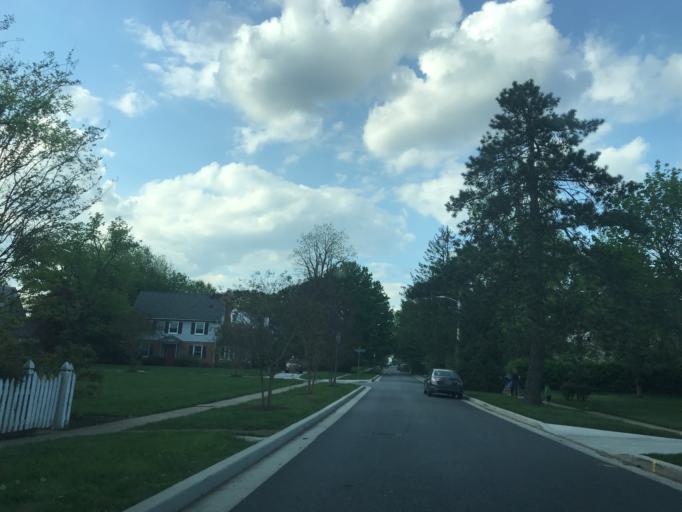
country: US
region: Maryland
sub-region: Baltimore County
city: Towson
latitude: 39.3726
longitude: -76.6154
